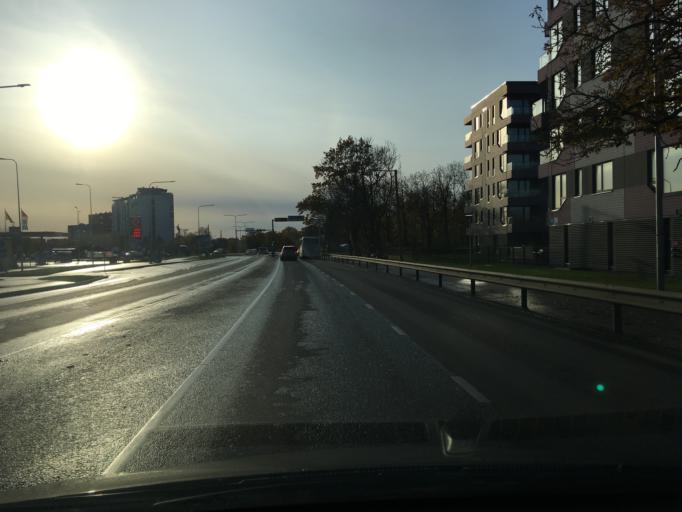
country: EE
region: Harju
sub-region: Viimsi vald
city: Viimsi
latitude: 59.4459
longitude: 24.8168
